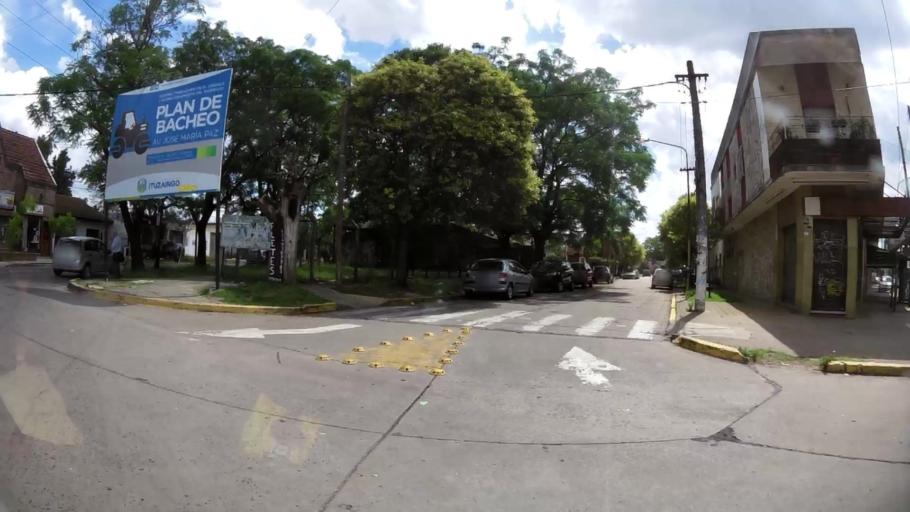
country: AR
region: Buenos Aires
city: Ituzaingo
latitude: -34.6482
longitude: -58.6646
